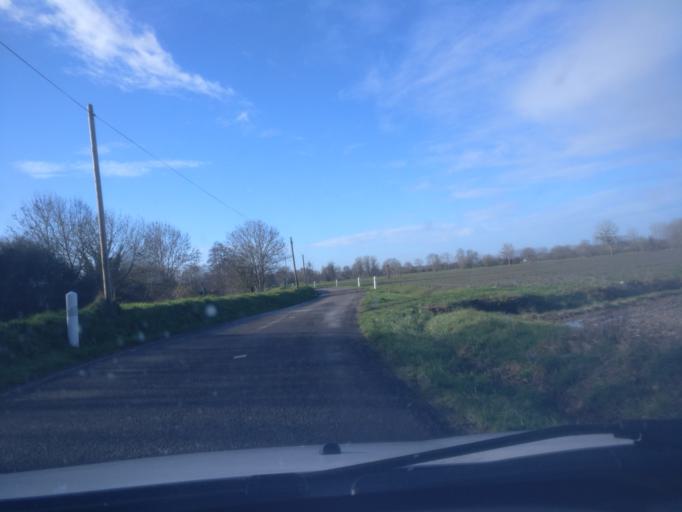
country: FR
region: Lower Normandy
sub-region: Departement de la Manche
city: Pontorson
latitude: 48.5423
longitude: -1.5135
